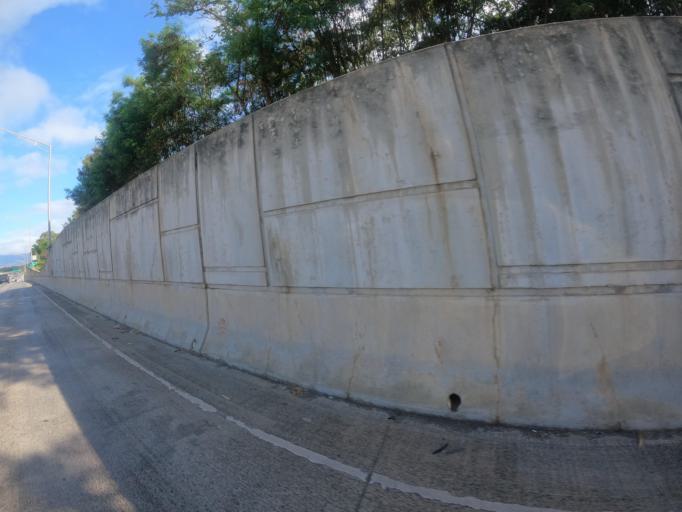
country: US
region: Hawaii
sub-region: Honolulu County
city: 'Aiea
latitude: 21.3895
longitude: -157.9426
